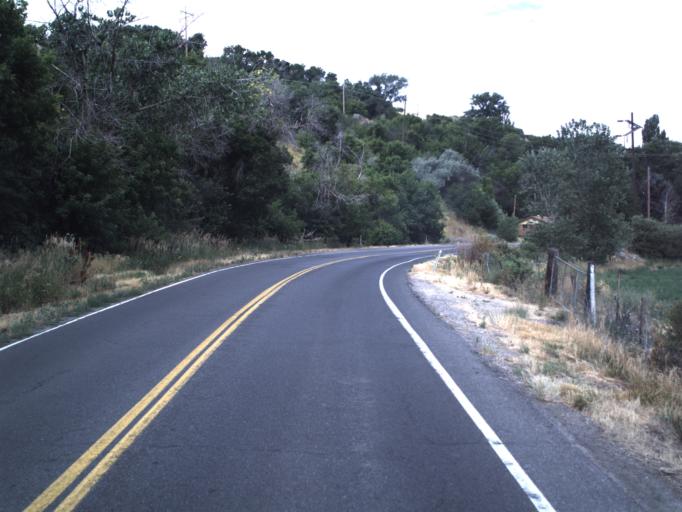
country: US
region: Utah
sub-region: Weber County
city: Riverdale
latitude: 41.1575
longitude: -112.0015
